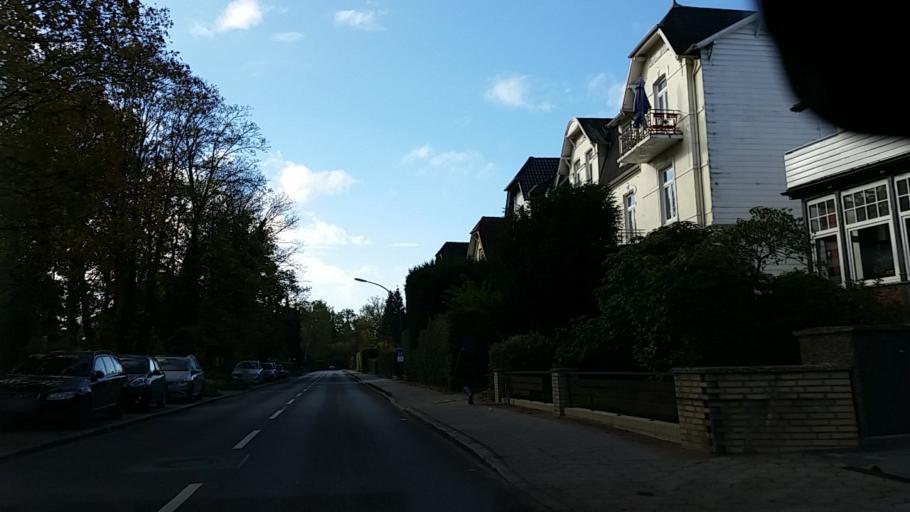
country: DE
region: Schleswig-Holstein
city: Halstenbek
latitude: 53.5636
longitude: 9.8259
